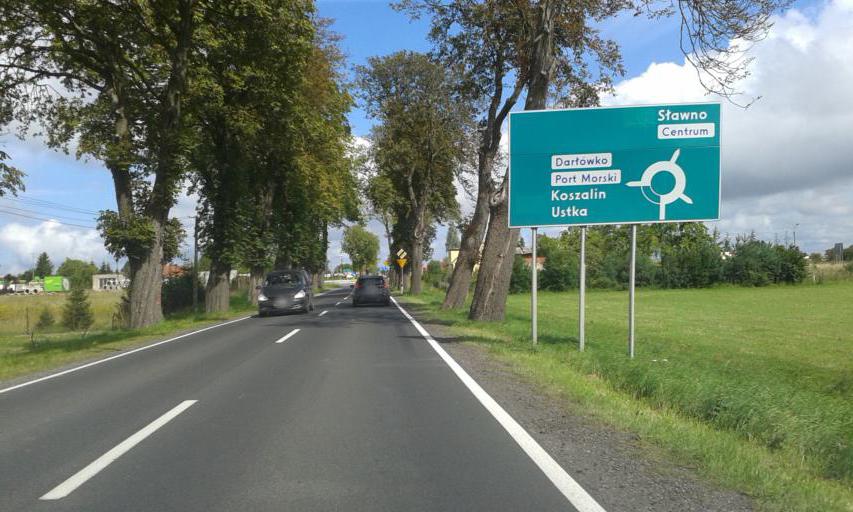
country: PL
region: West Pomeranian Voivodeship
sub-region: Powiat slawienski
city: Darlowo
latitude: 54.4076
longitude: 16.4104
